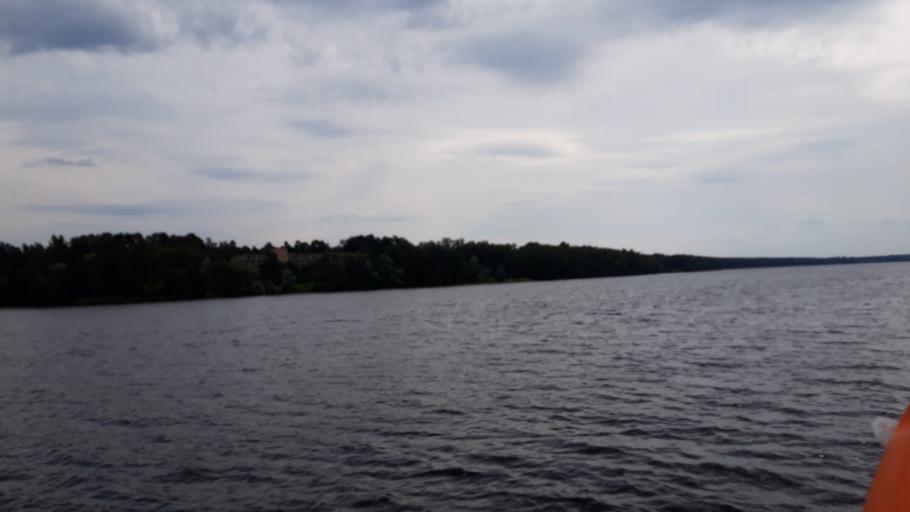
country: RU
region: Tverskaya
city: Konakovo
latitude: 56.6935
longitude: 36.6978
